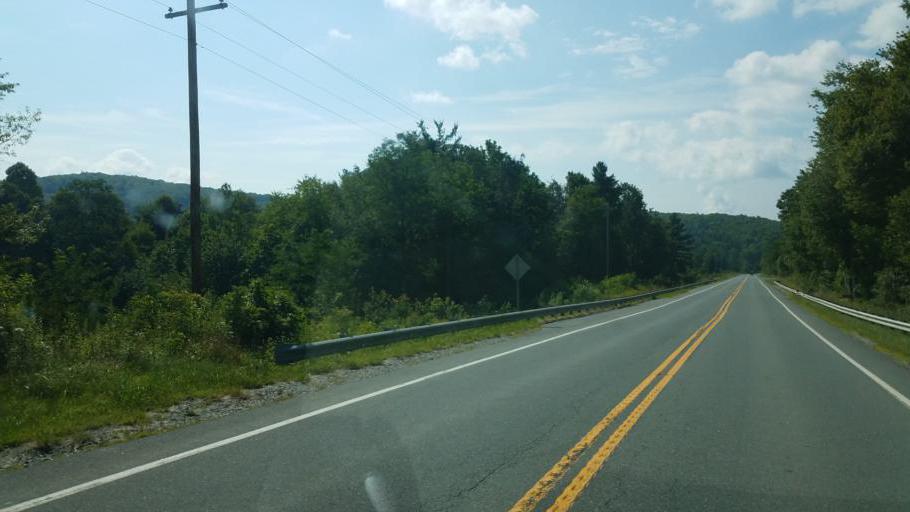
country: US
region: North Carolina
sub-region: Avery County
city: Newland
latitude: 35.9646
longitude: -81.8924
